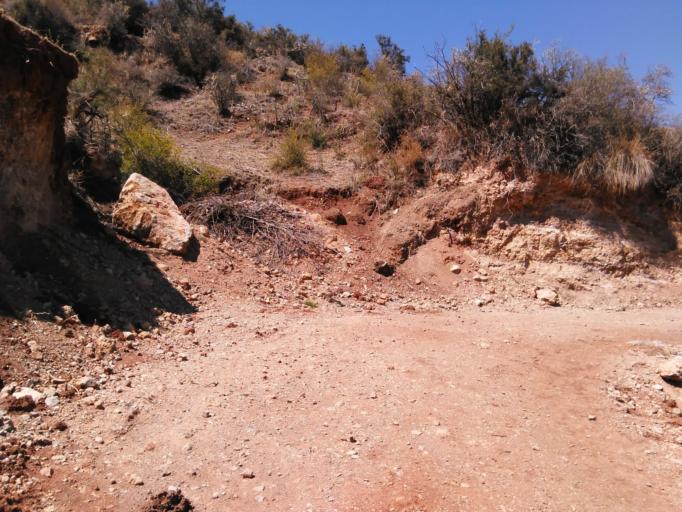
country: PE
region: Ayacucho
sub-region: Provincia de Victor Fajardo
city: Canaria
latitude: -13.8854
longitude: -73.9447
